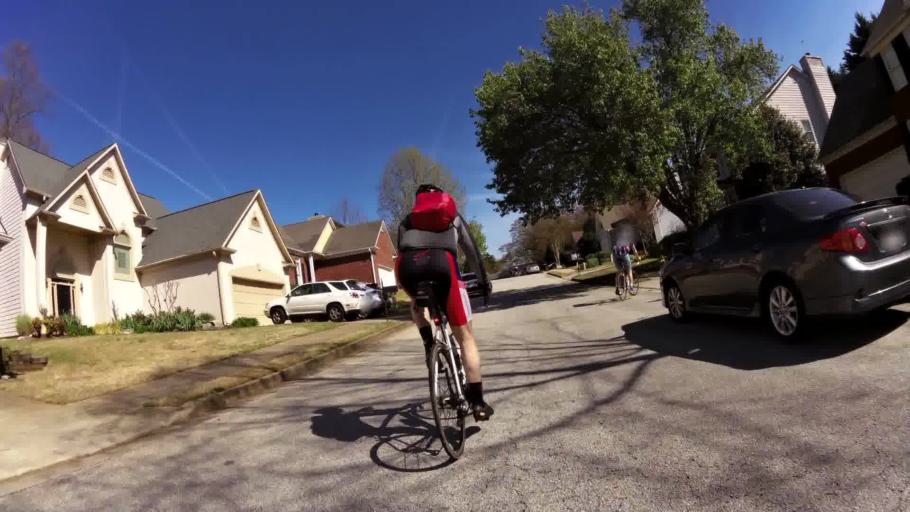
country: US
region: Georgia
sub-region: DeKalb County
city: Clarkston
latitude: 33.8235
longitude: -84.2668
